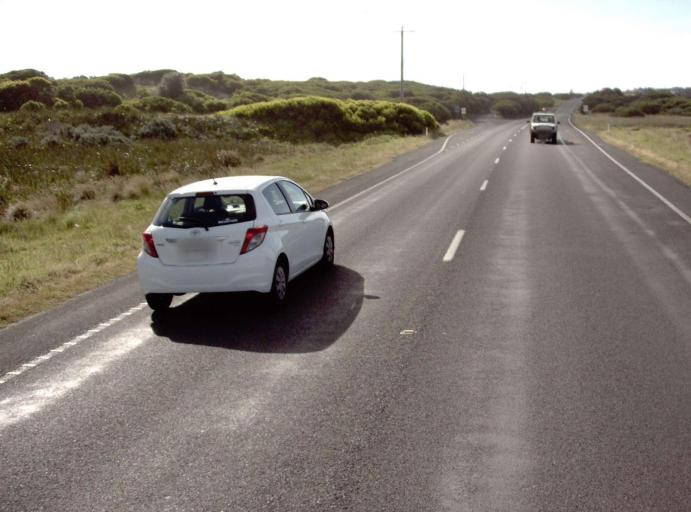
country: AU
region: Victoria
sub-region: Bass Coast
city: North Wonthaggi
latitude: -38.5559
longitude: 145.4861
